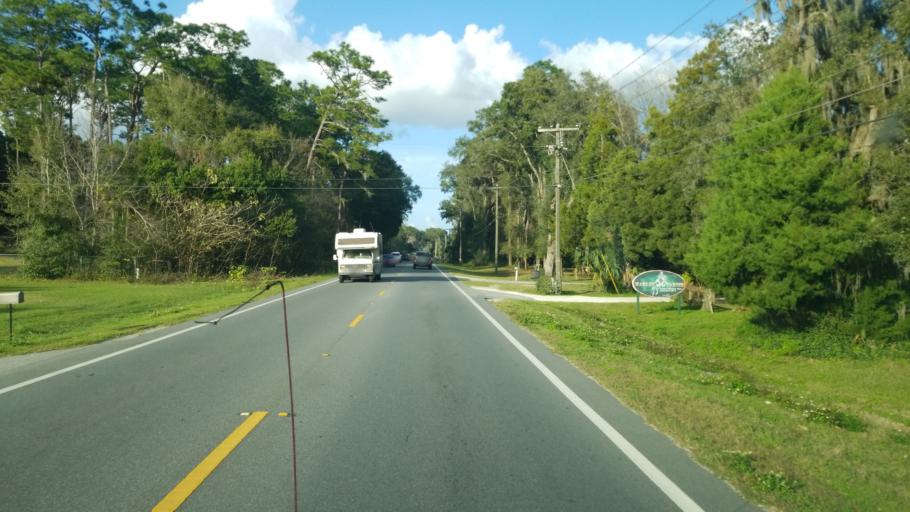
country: US
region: Florida
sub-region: Marion County
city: Ocala
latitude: 29.2335
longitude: -82.1209
